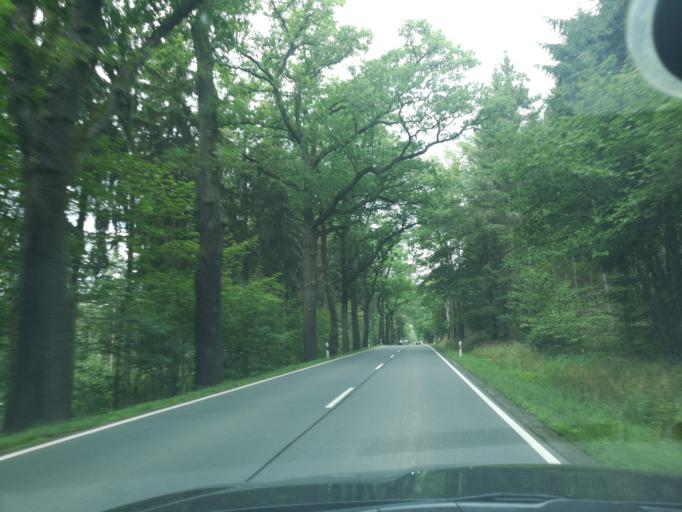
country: DE
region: Saxony
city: Eichigt
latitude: 50.3755
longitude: 12.2060
